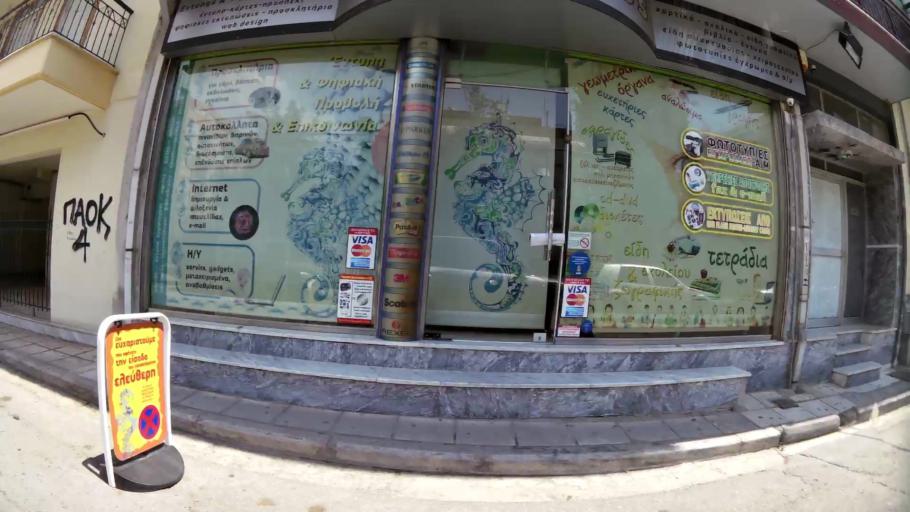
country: GR
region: Central Macedonia
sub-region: Nomos Thessalonikis
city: Ampelokipoi
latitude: 40.6576
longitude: 22.9221
